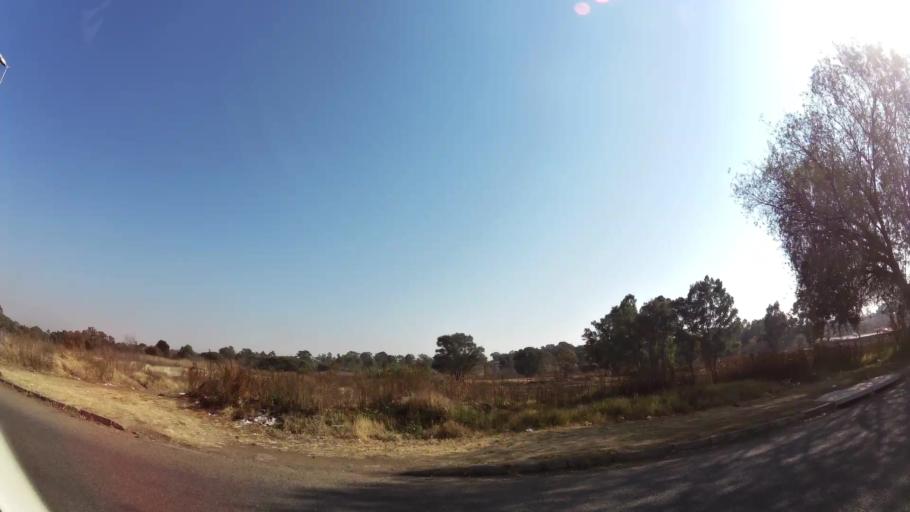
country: ZA
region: Gauteng
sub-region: Ekurhuleni Metropolitan Municipality
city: Boksburg
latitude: -26.2169
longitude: 28.2594
